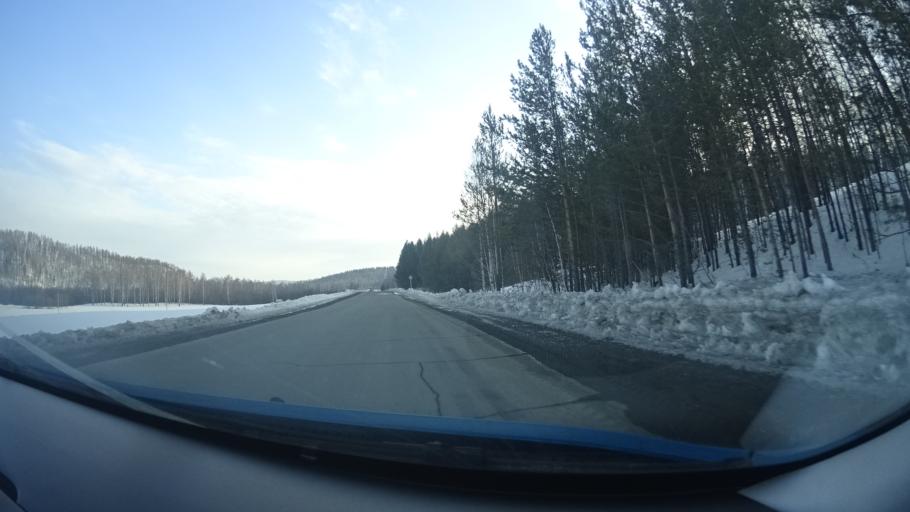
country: RU
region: Bashkortostan
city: Abzakovo
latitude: 53.4518
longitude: 58.3126
